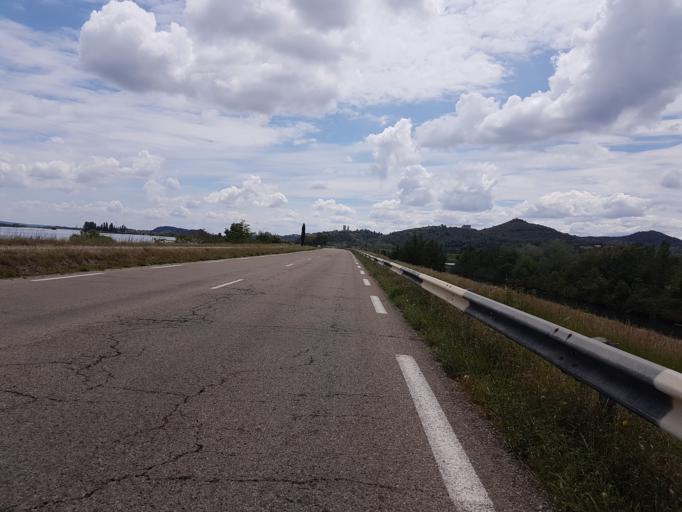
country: FR
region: Languedoc-Roussillon
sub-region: Departement du Gard
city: Vallabregues
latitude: 43.8546
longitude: 4.6180
